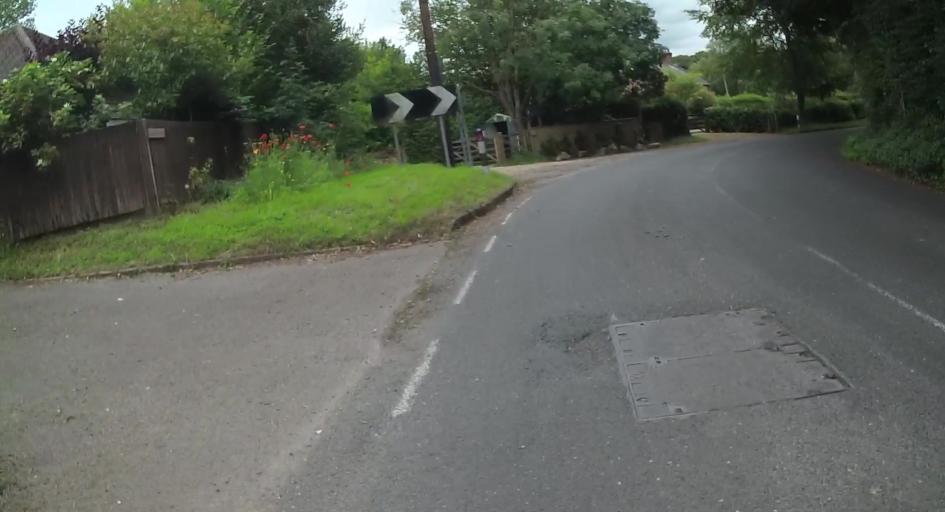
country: GB
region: England
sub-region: Hampshire
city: Swanmore
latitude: 51.0491
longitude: -1.1614
